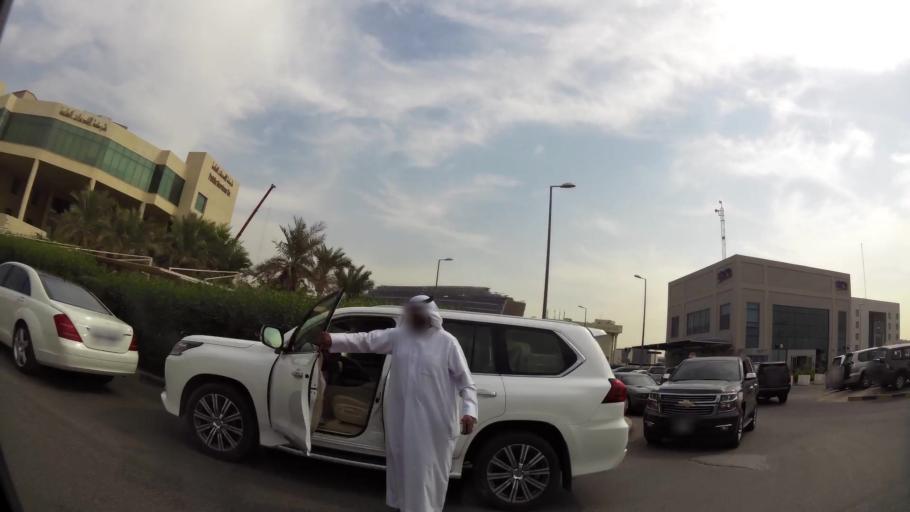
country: KW
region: Al Farwaniyah
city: Janub as Surrah
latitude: 29.2725
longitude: 48.0162
